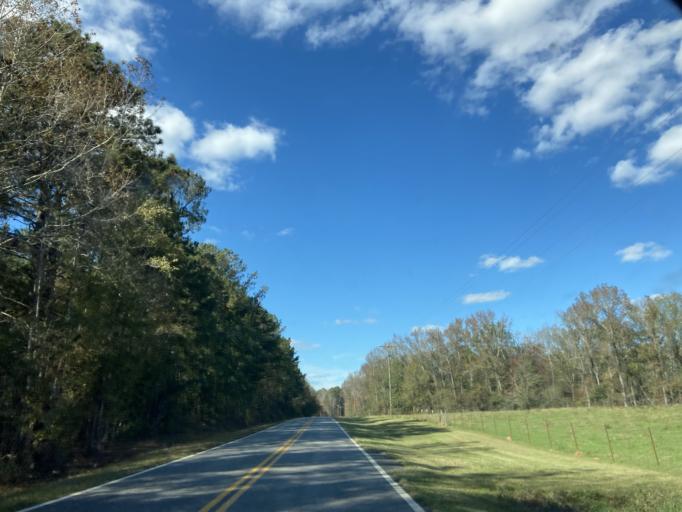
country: US
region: Georgia
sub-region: Jones County
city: Gray
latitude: 32.9412
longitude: -83.5111
